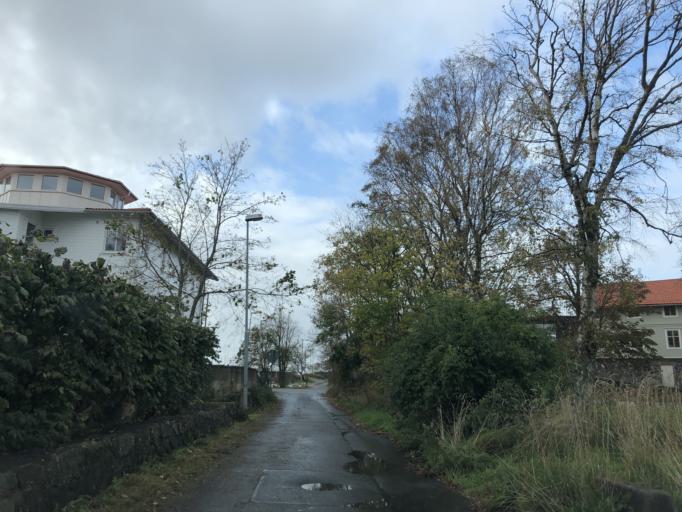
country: SE
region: Vaestra Goetaland
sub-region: Goteborg
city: Majorna
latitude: 57.6694
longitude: 11.8512
